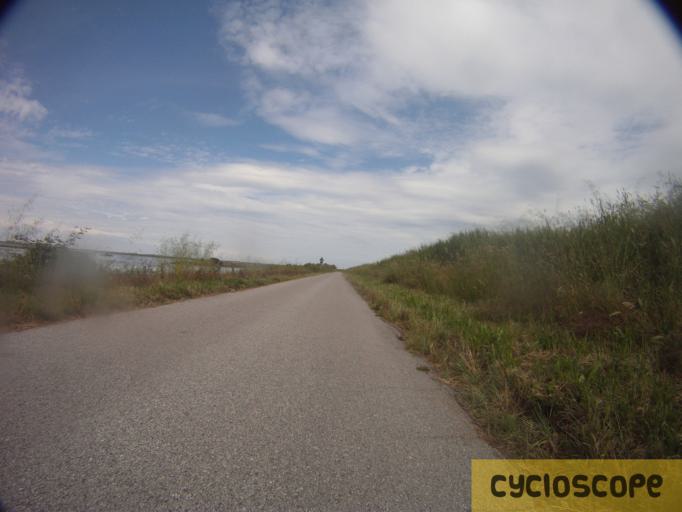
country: IT
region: Veneto
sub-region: Provincia di Rovigo
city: Rosolina
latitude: 45.0957
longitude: 12.2959
